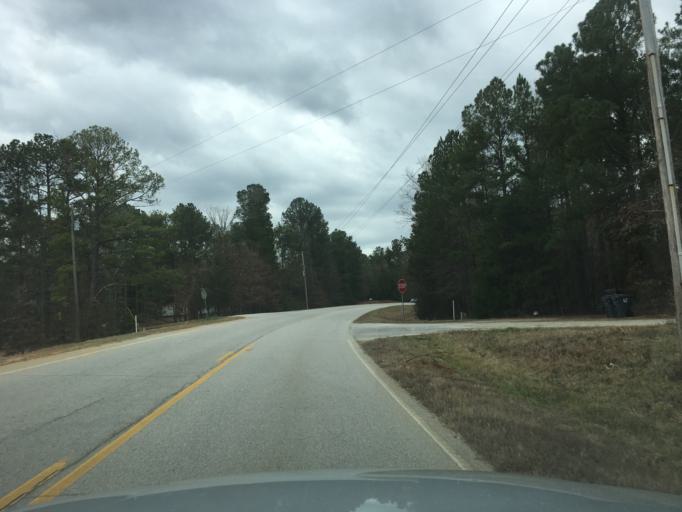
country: US
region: Georgia
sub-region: Lincoln County
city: Lincolnton
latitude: 33.8419
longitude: -82.4084
